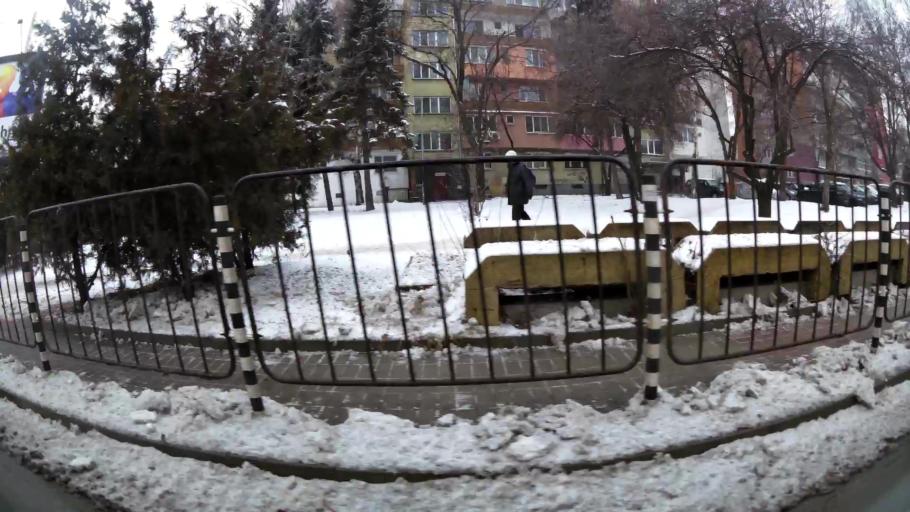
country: BG
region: Sofia-Capital
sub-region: Stolichna Obshtina
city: Sofia
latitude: 42.7132
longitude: 23.3151
